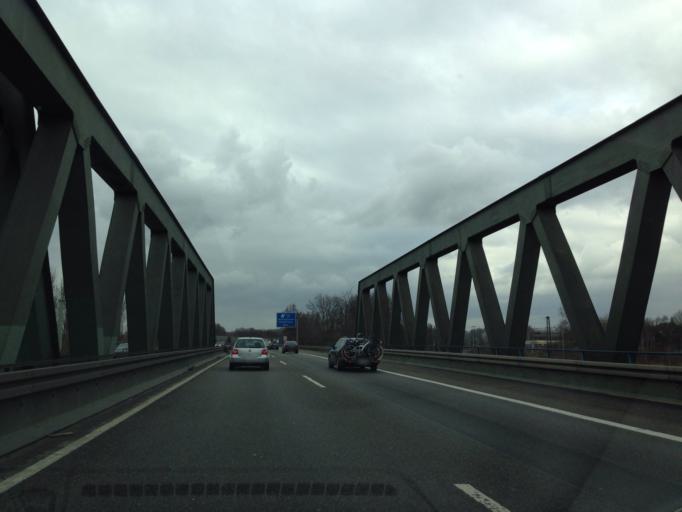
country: DE
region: North Rhine-Westphalia
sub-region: Regierungsbezirk Arnsberg
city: Herne
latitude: 51.5581
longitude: 7.1952
